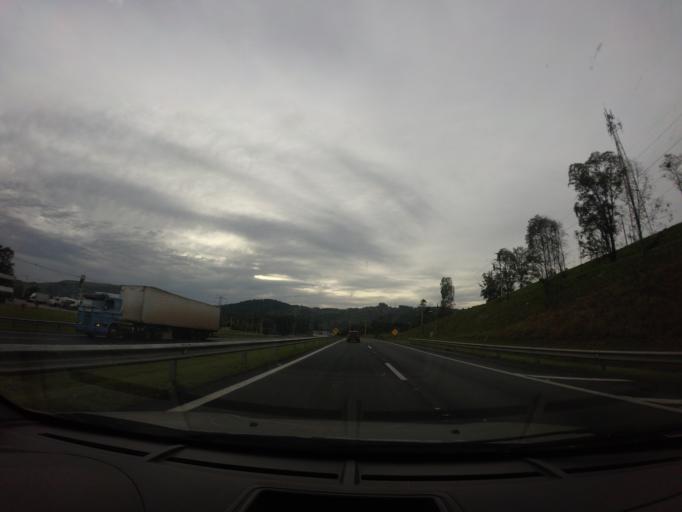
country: BR
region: Sao Paulo
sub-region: Valinhos
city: Valinhos
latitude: -22.9124
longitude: -46.9662
